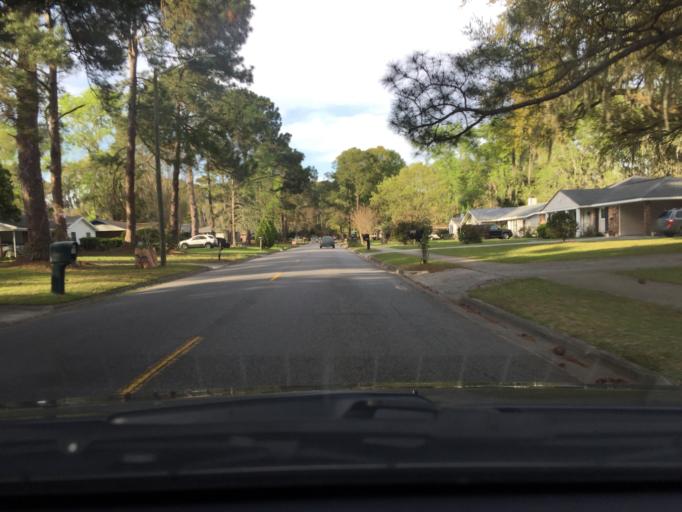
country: US
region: Georgia
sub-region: Chatham County
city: Montgomery
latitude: 31.9903
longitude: -81.1445
